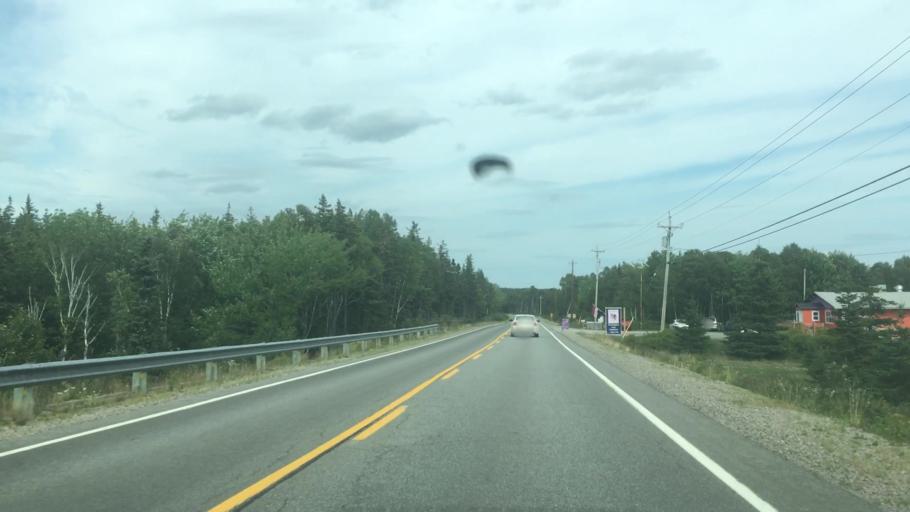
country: CA
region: Nova Scotia
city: Sydney Mines
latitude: 46.5058
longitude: -60.4338
